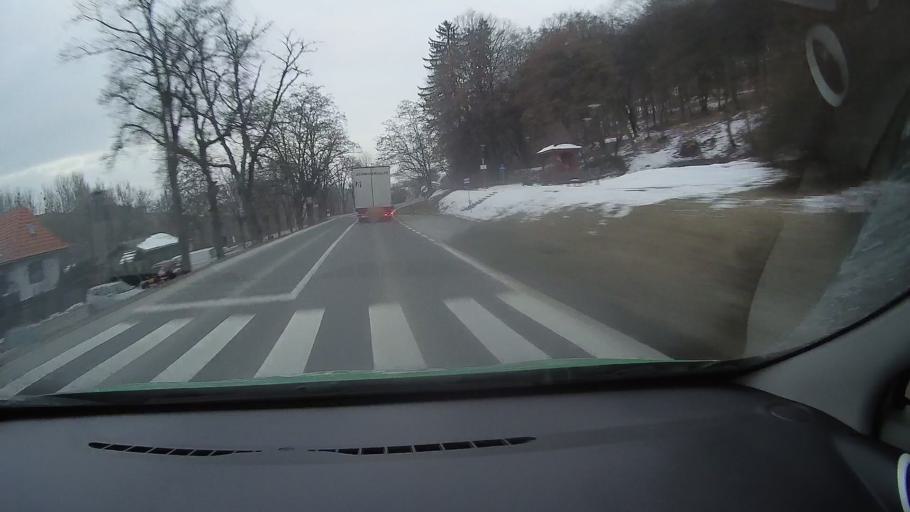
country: RO
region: Harghita
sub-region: Municipiul Odorheiu Secuiesc
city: Odorheiu Secuiesc
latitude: 46.3312
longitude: 25.2739
